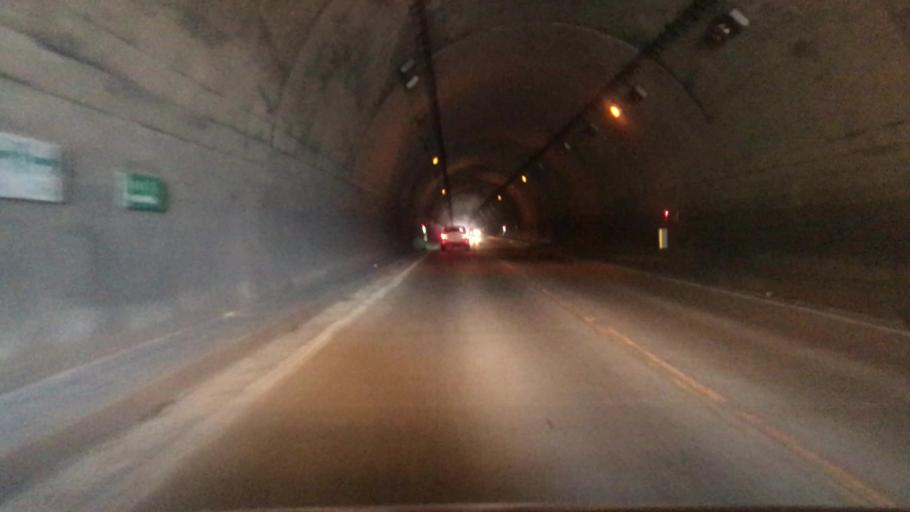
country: JP
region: Hyogo
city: Toyooka
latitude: 35.5583
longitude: 134.8285
